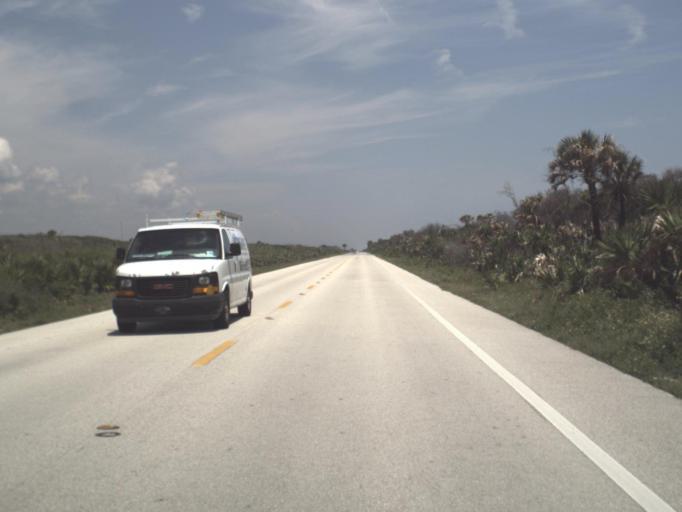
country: US
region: Florida
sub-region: Saint Johns County
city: Palm Valley
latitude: 30.0944
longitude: -81.3401
